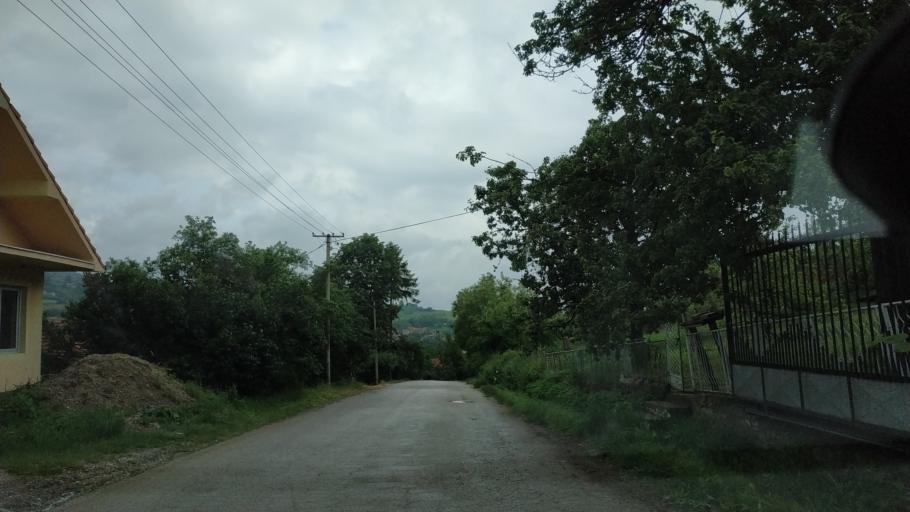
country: RS
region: Central Serbia
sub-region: Toplicki Okrug
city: Prokuplje
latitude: 43.3948
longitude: 21.5542
